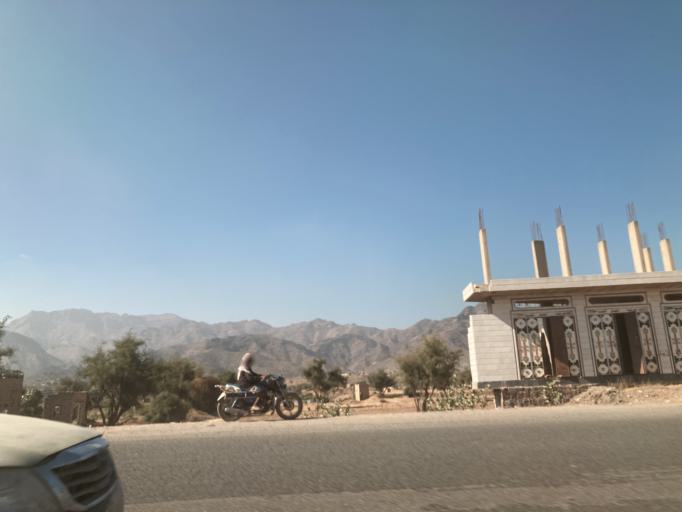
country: YE
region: Ad Dali'
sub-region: Qa'atabah
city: Qa`tabah
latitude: 13.8096
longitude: 44.7226
